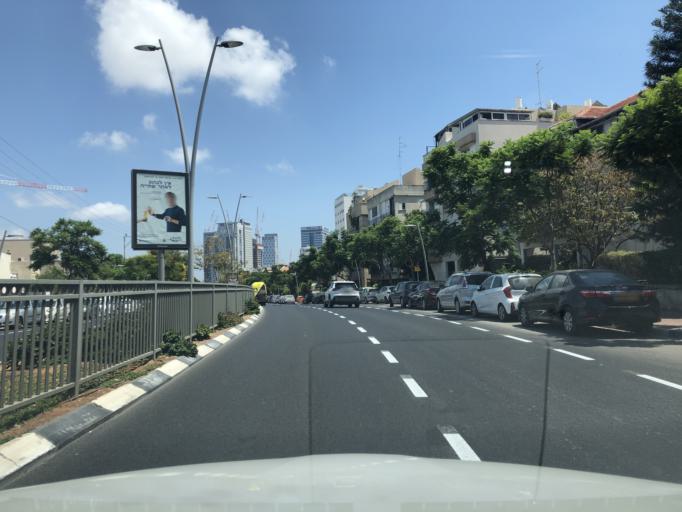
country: IL
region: Tel Aviv
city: Ramat Gan
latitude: 32.0912
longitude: 34.8137
